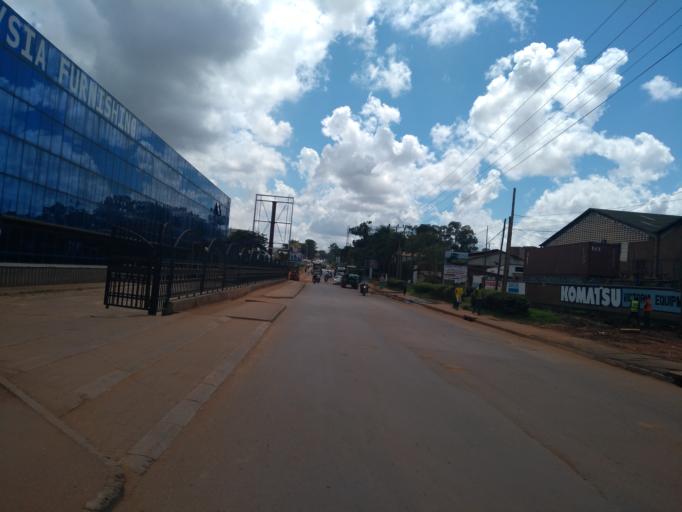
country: UG
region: Central Region
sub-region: Kampala District
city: Kampala
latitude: 0.3145
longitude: 32.6111
